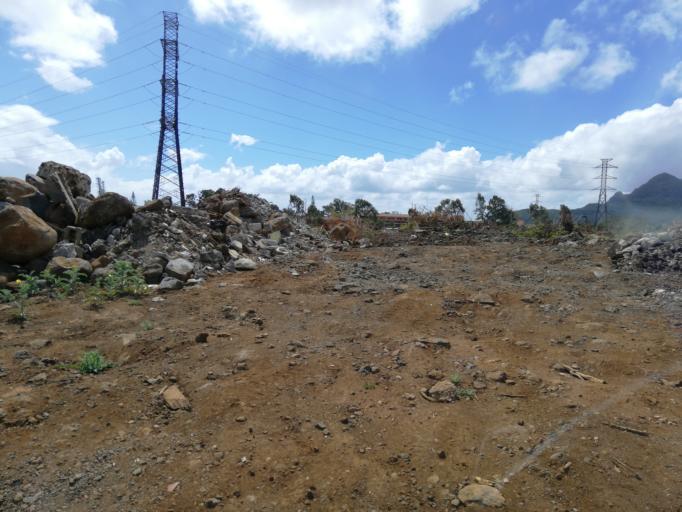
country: MU
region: Plaines Wilhems
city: Ebene
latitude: -20.2408
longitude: 57.4788
